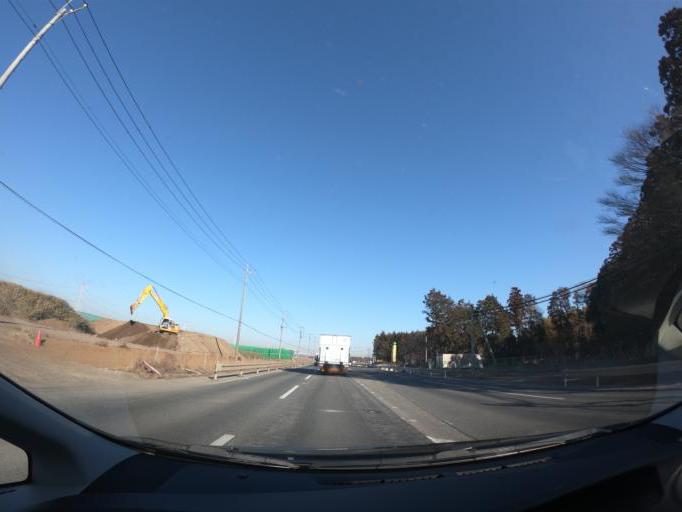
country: JP
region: Ibaraki
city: Mitsukaido
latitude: 36.0656
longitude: 140.0423
